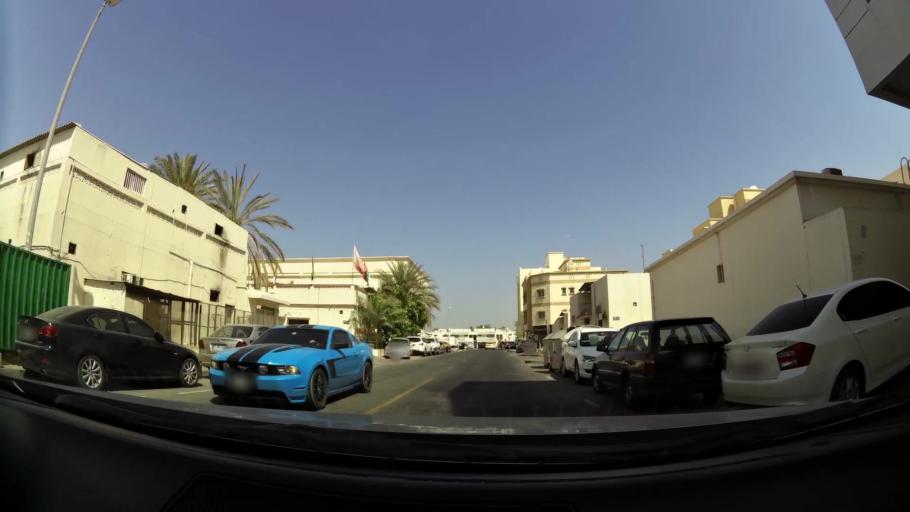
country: AE
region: Ash Shariqah
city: Sharjah
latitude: 25.2316
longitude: 55.2748
